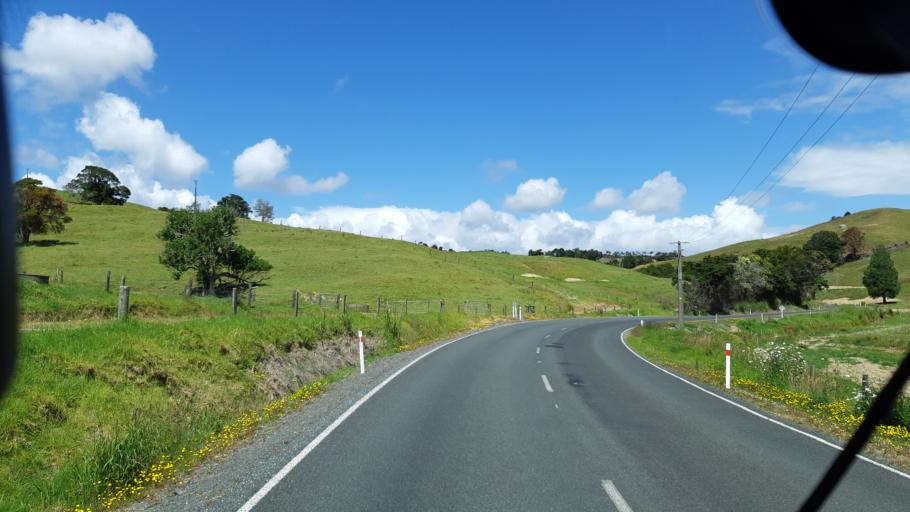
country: NZ
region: Northland
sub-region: Far North District
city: Kaitaia
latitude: -35.2701
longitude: 173.4898
